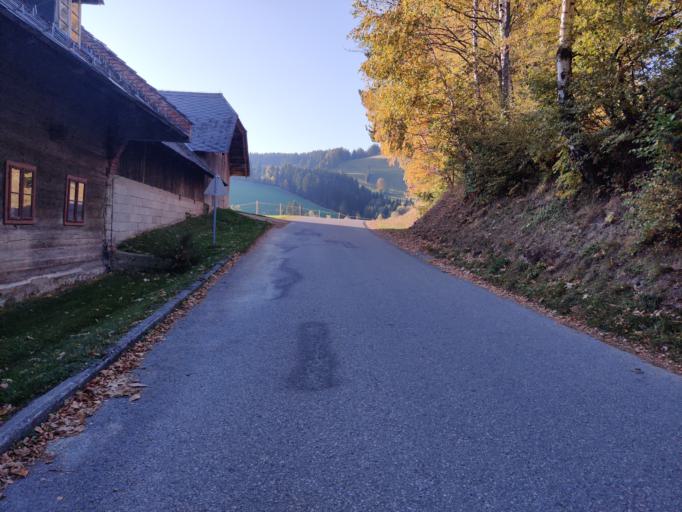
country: AT
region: Styria
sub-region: Politischer Bezirk Hartberg-Fuerstenfeld
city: Sankt Jakob im Walde
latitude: 47.4749
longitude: 15.7956
